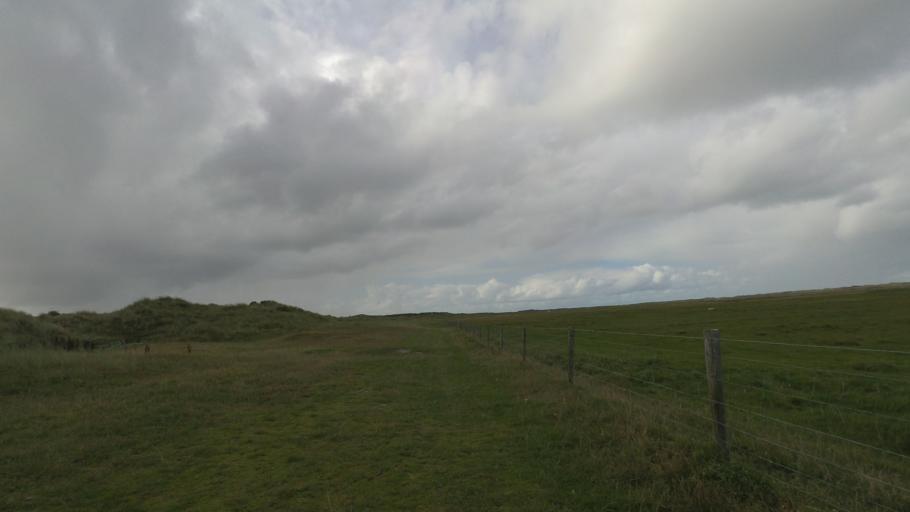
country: NL
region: Friesland
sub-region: Gemeente Ameland
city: Nes
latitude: 53.4510
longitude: 5.8562
